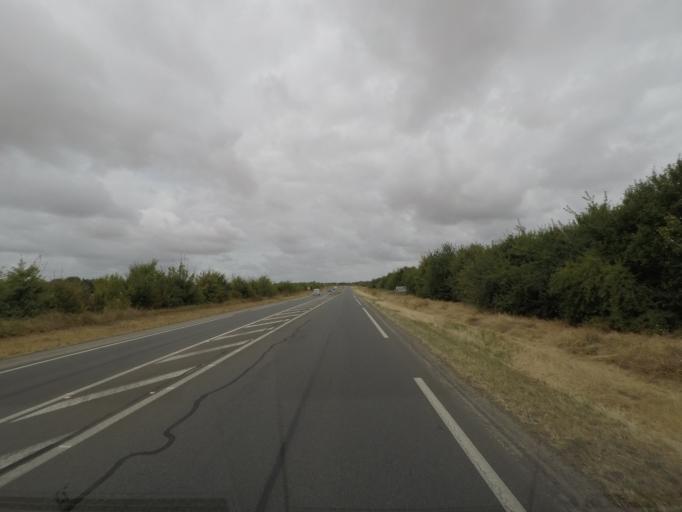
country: FR
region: Poitou-Charentes
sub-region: Departement des Deux-Sevres
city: Thorigne
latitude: 46.2832
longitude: -0.2605
